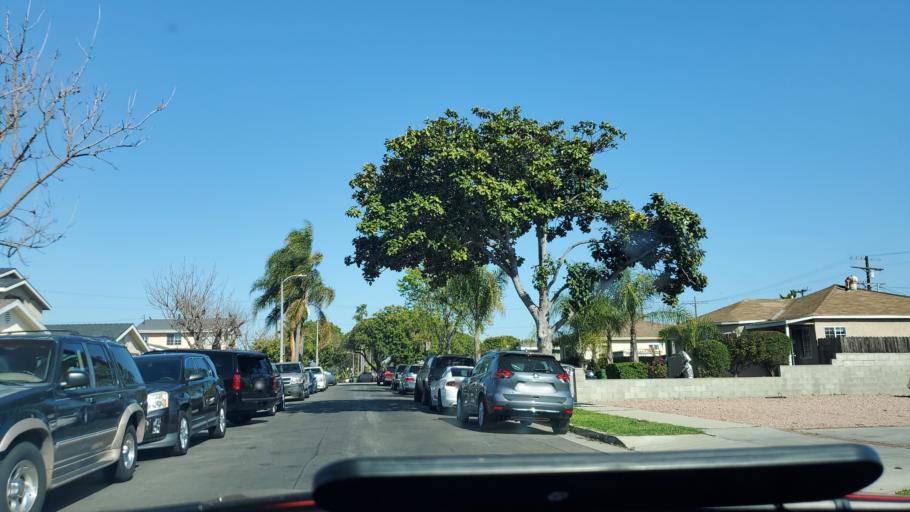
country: US
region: California
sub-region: Los Angeles County
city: Lomita
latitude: 33.7869
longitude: -118.2790
